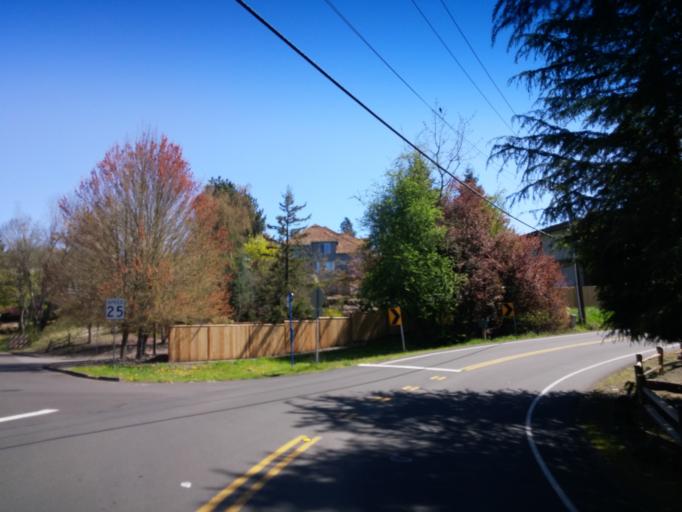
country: US
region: Oregon
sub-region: Washington County
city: West Haven
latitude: 45.5231
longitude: -122.7726
